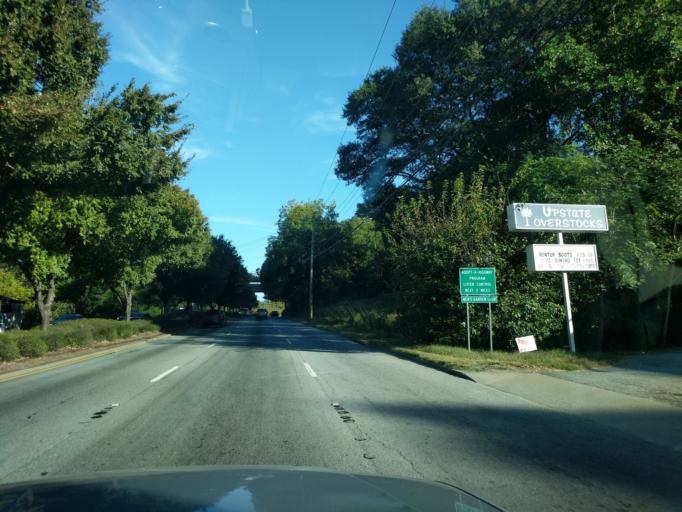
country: US
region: South Carolina
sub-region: Spartanburg County
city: Spartanburg
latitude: 34.9646
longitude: -81.9299
